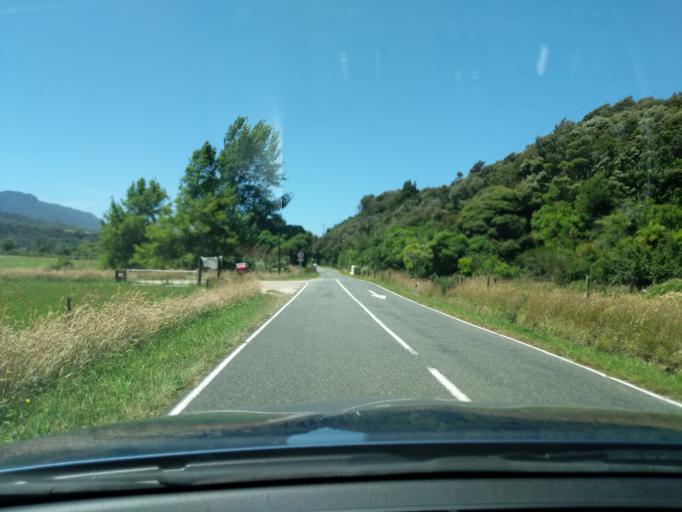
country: NZ
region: Tasman
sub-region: Tasman District
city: Takaka
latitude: -40.7282
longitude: 172.5842
